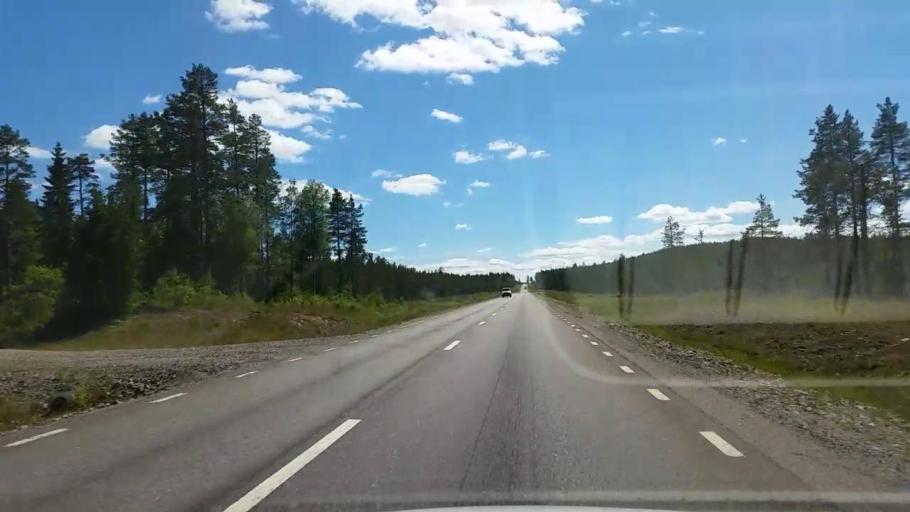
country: SE
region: Gaevleborg
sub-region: Bollnas Kommun
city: Vittsjo
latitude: 61.1204
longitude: 15.8657
